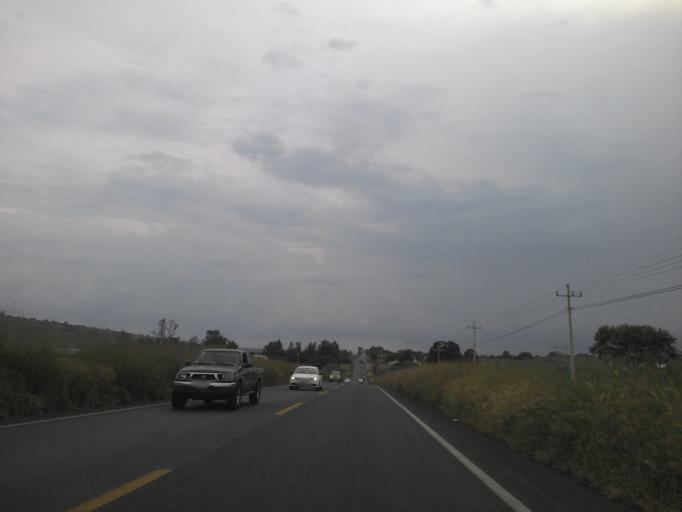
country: MX
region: Jalisco
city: Zapotlanejo
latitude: 20.6900
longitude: -102.9878
